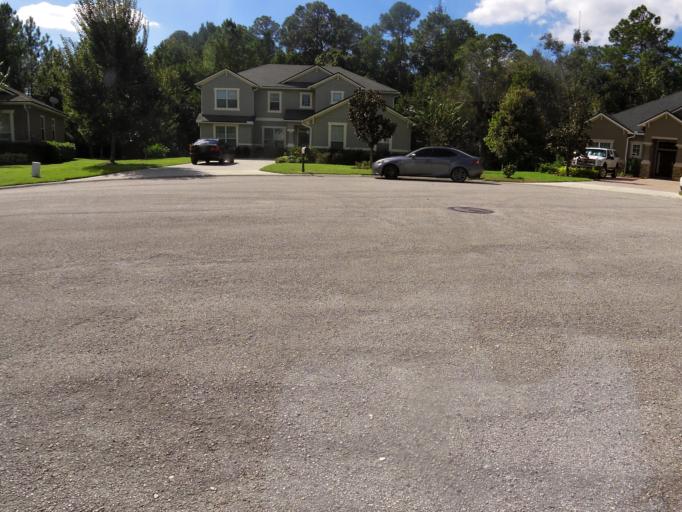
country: US
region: Florida
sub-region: Saint Johns County
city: Fruit Cove
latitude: 30.0695
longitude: -81.6448
